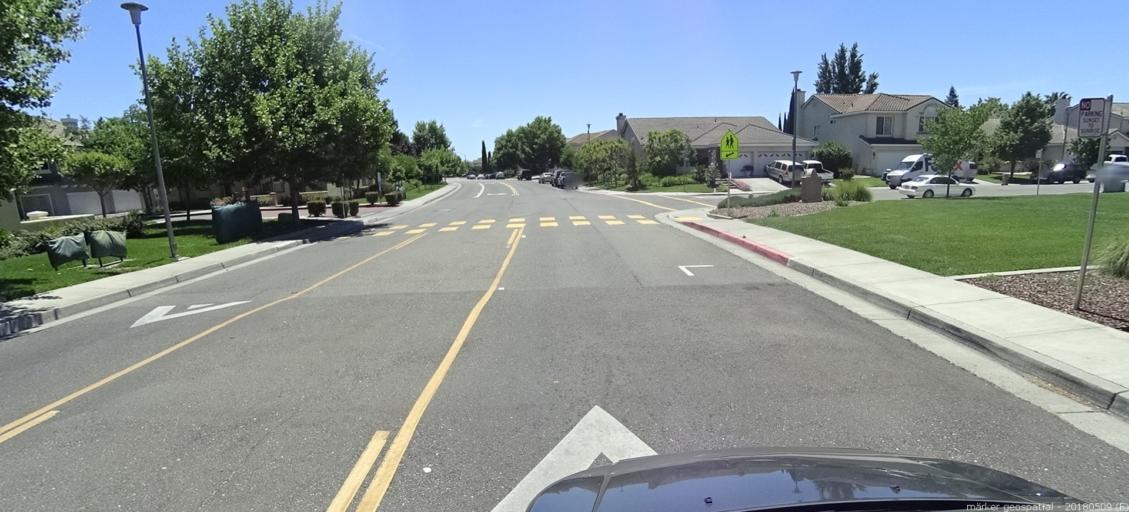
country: US
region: California
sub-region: Sacramento County
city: Sacramento
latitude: 38.6415
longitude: -121.5108
